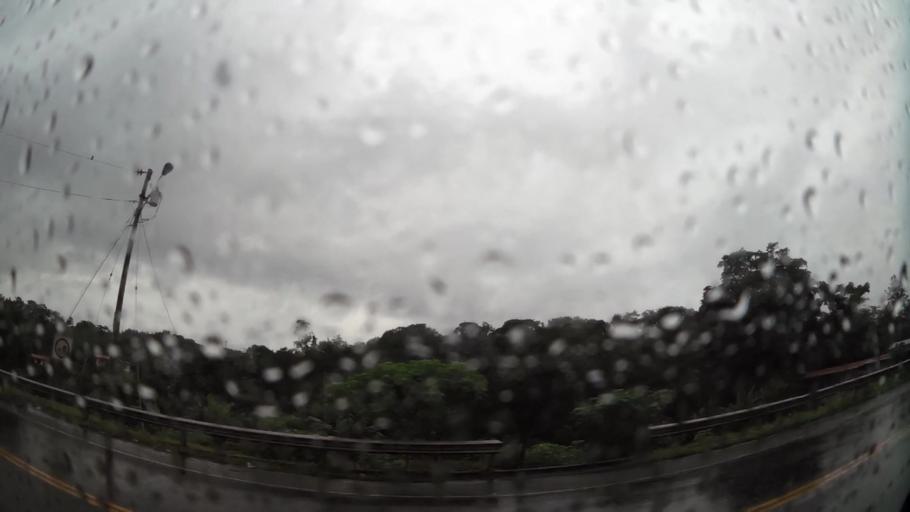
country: PA
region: Colon
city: Quebrada Bonita Adentro
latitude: 9.2863
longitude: -79.7176
